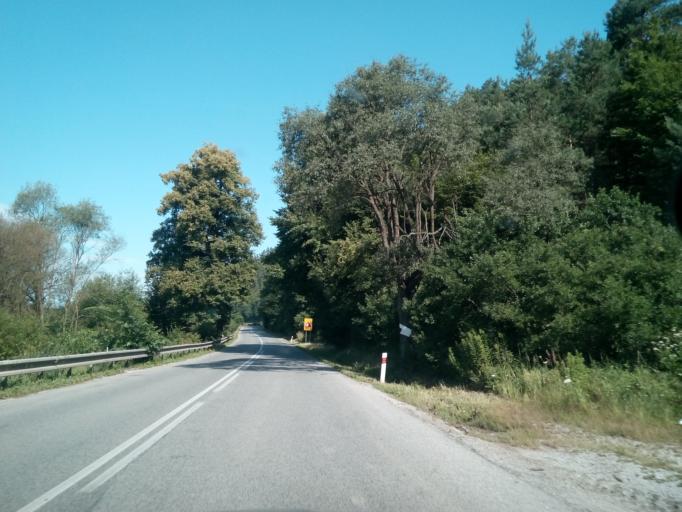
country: SK
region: Kosicky
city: Krompachy
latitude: 48.9332
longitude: 20.8394
